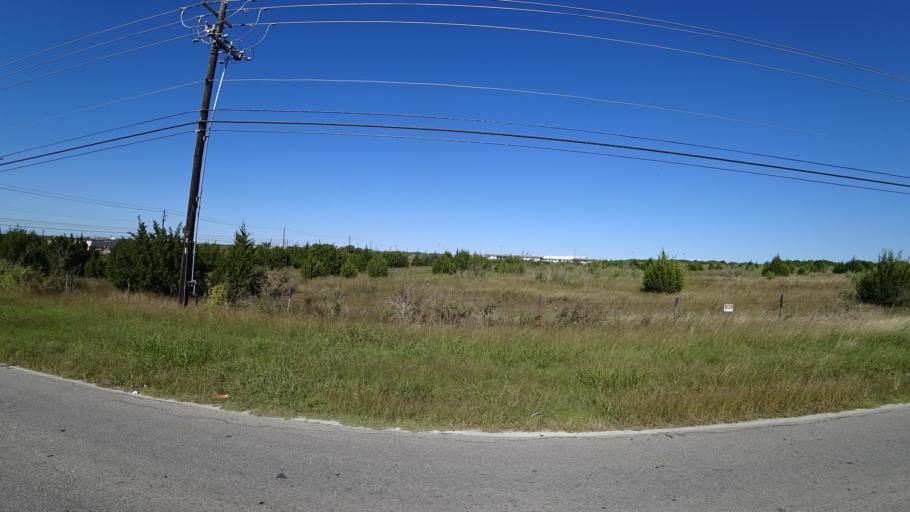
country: US
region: Texas
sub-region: Travis County
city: Hornsby Bend
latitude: 30.2859
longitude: -97.6305
